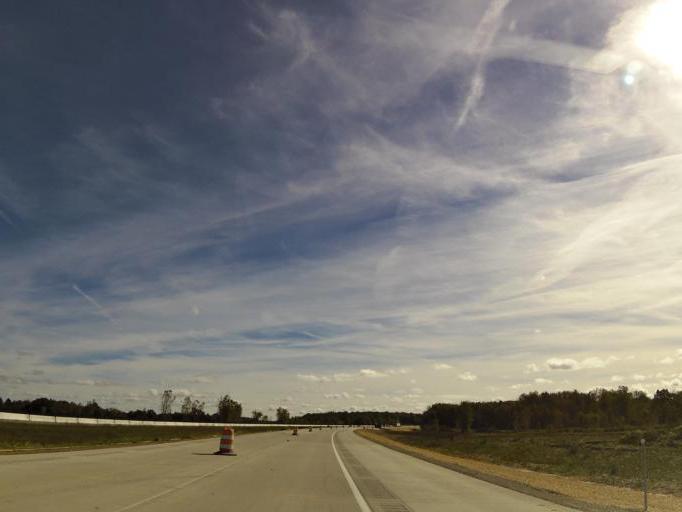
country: US
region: Michigan
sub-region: Macomb County
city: Memphis
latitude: 42.9800
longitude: -82.7616
